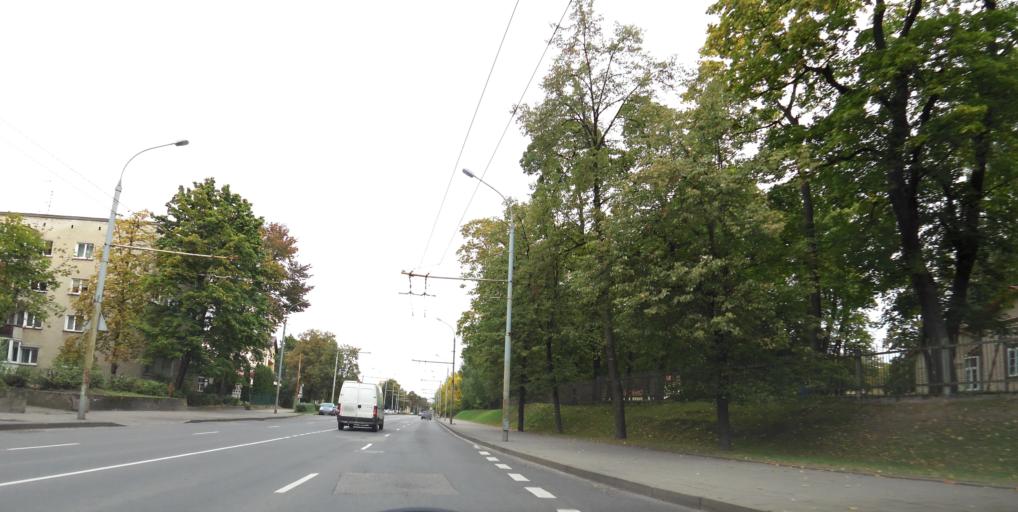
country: LT
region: Vilnius County
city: Rasos
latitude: 54.6971
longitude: 25.3087
